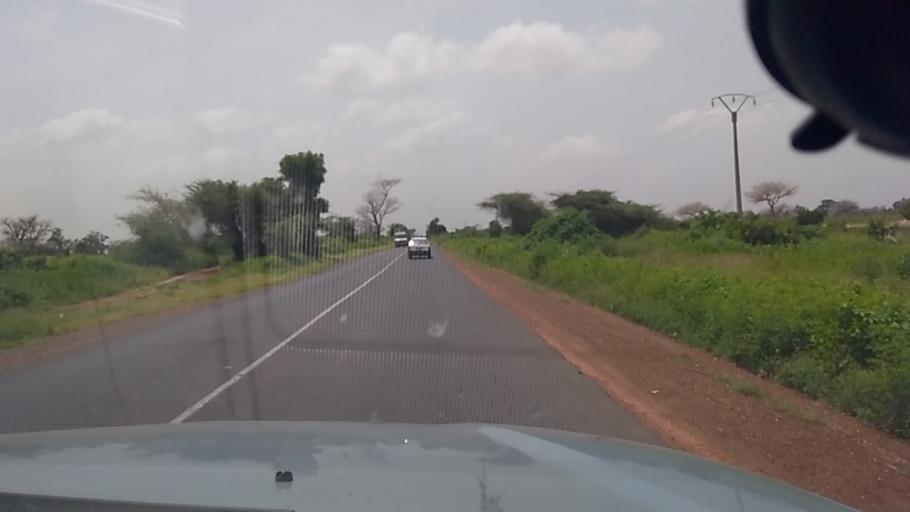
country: SN
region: Thies
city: Mekhe
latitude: 15.0353
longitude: -16.7173
